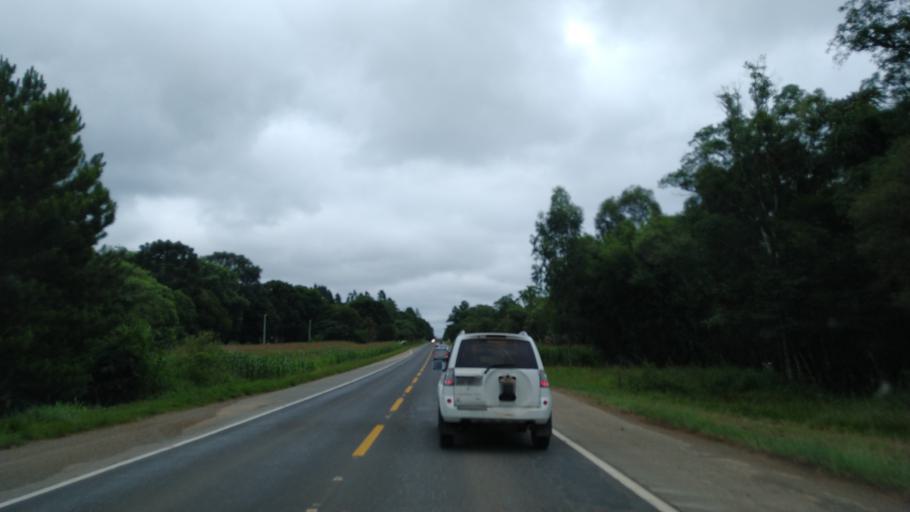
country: BR
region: Santa Catarina
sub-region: Tres Barras
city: Tres Barras
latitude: -26.1790
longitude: -50.1893
